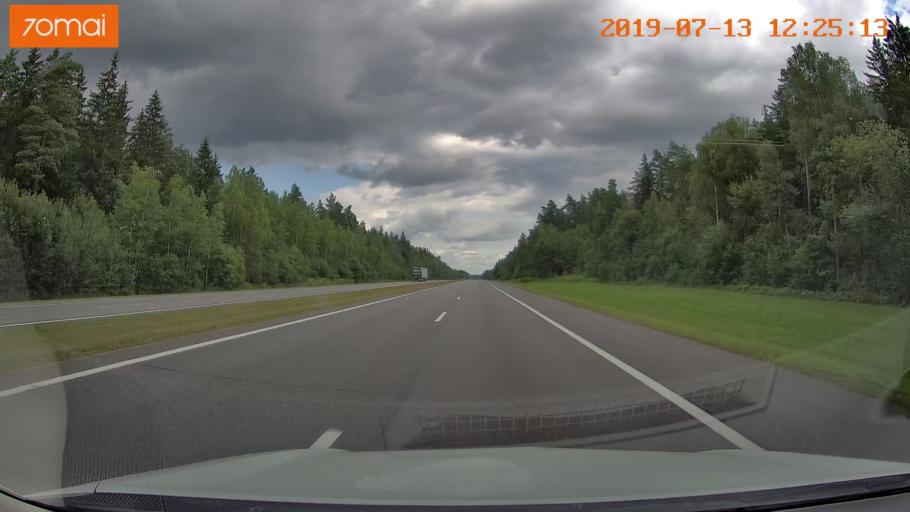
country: BY
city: Michanovichi
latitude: 53.7706
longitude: 27.6876
